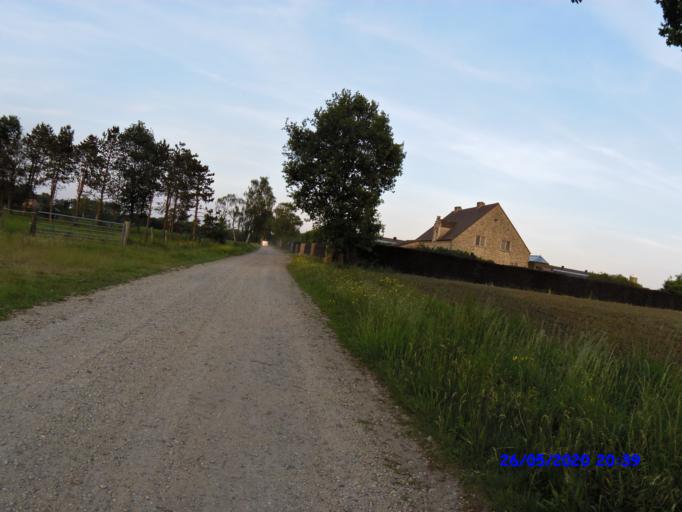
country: BE
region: Flanders
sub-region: Provincie Antwerpen
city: Geel
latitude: 51.1895
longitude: 5.0028
